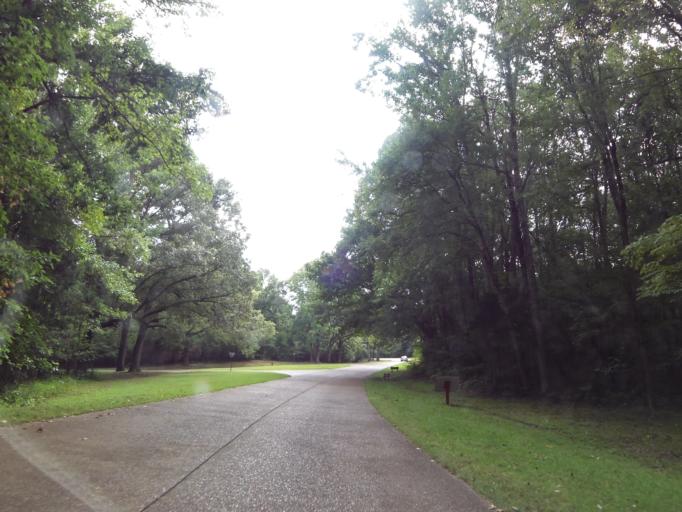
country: US
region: Tennessee
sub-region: Hardin County
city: Crump
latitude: 35.1307
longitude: -88.3560
